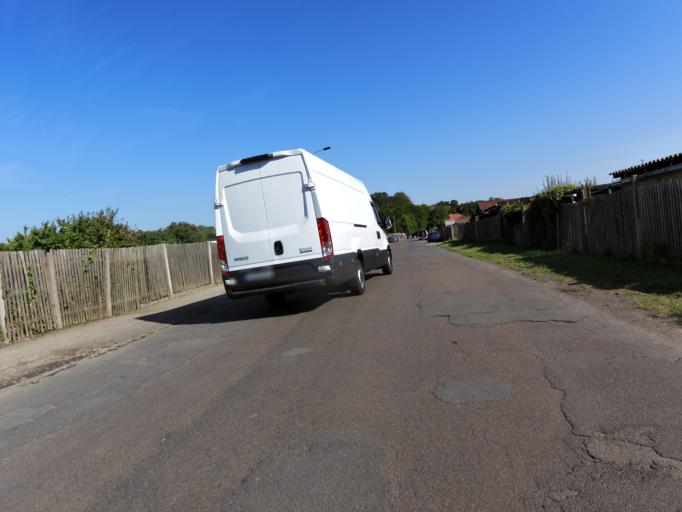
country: DE
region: Saxony
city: Leipzig
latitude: 51.3626
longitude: 12.4186
